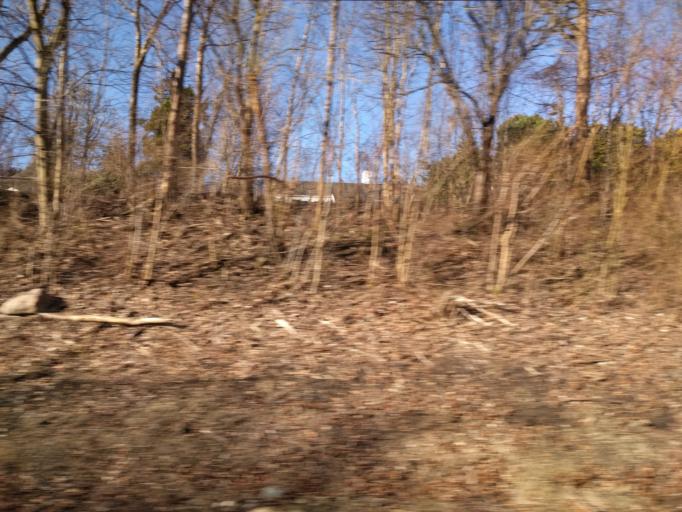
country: DK
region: Capital Region
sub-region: Rudersdal Kommune
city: Trorod
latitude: 55.8330
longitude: 12.5675
